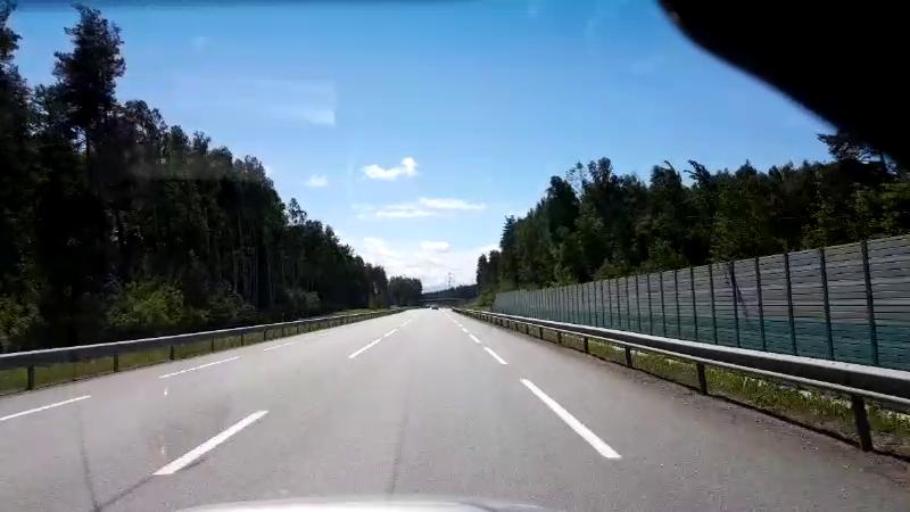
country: LV
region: Saulkrastu
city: Saulkrasti
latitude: 57.2488
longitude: 24.4279
